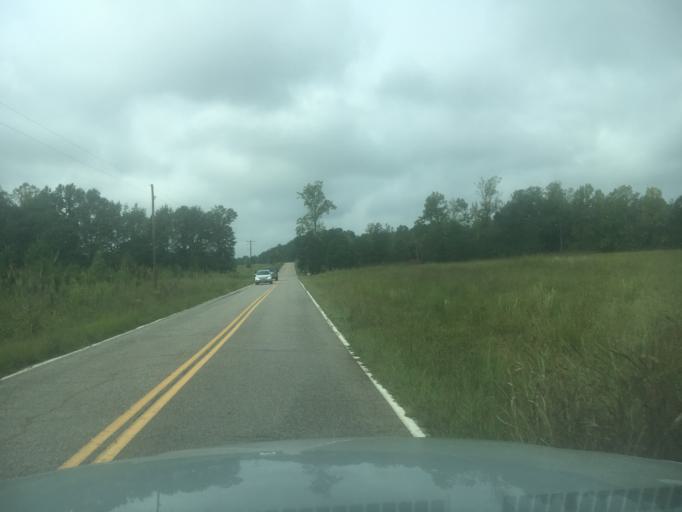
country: US
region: South Carolina
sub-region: Spartanburg County
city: Inman
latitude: 35.1747
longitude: -82.0553
